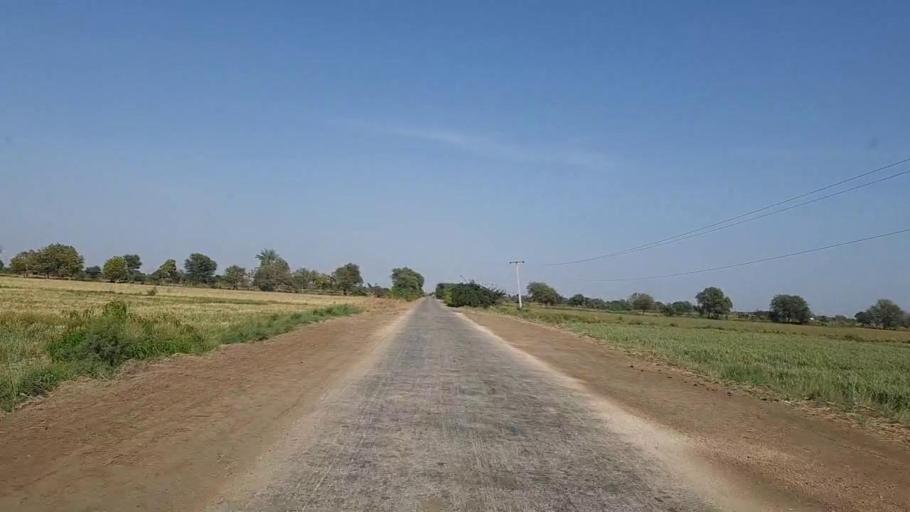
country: PK
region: Sindh
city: Kotri
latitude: 25.1661
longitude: 68.2761
